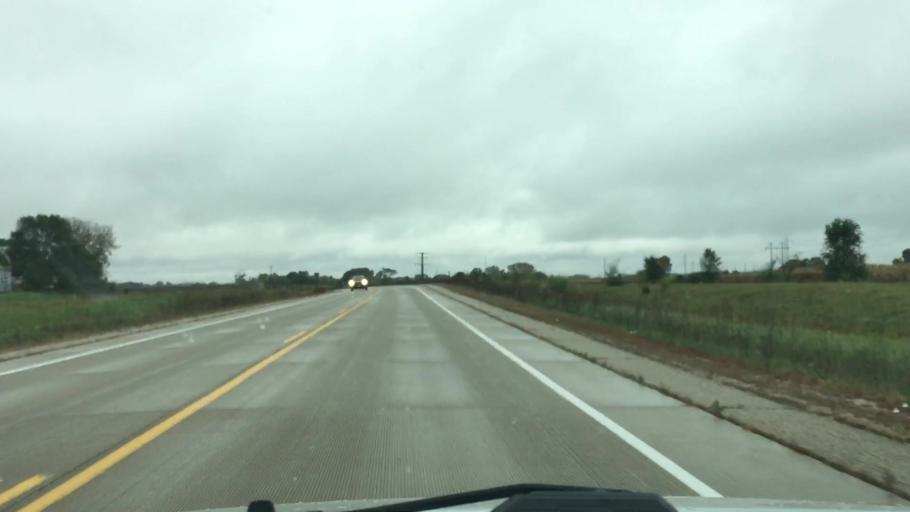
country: US
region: Wisconsin
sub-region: Walworth County
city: Whitewater
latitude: 42.8192
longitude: -88.7223
